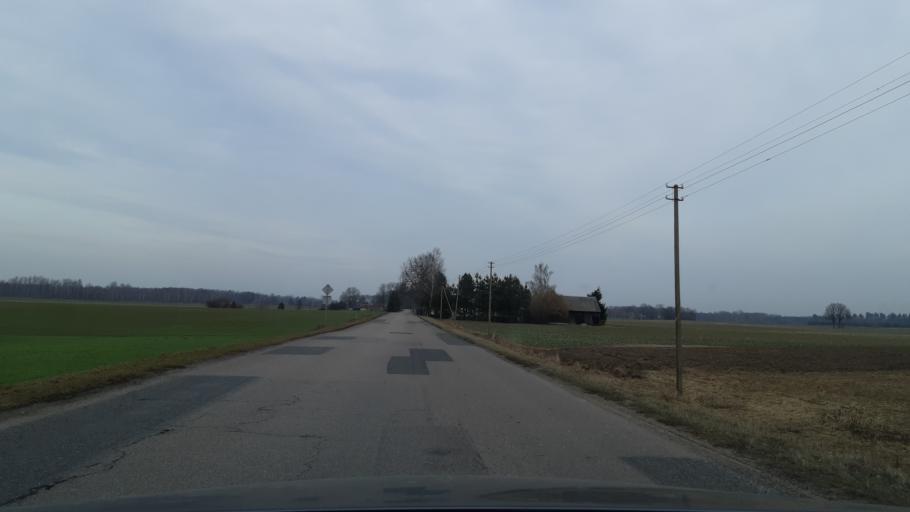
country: LT
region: Marijampoles apskritis
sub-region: Marijampole Municipality
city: Marijampole
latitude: 54.7174
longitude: 23.3322
